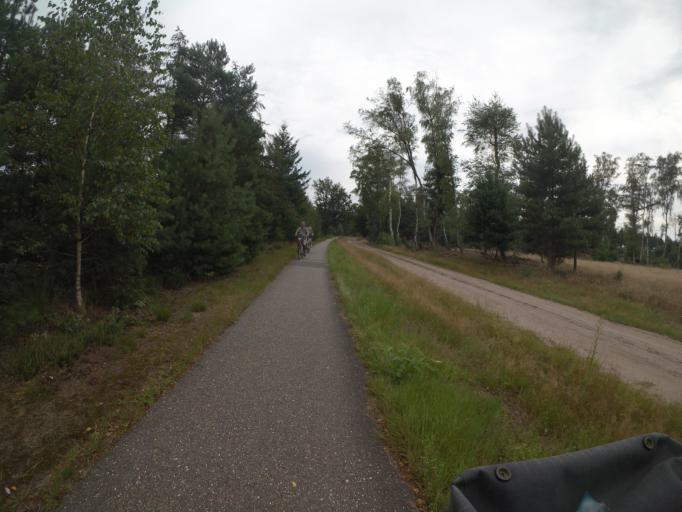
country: NL
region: North Brabant
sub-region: Gemeente Valkenswaard
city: Valkenswaard
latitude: 51.3207
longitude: 5.5024
